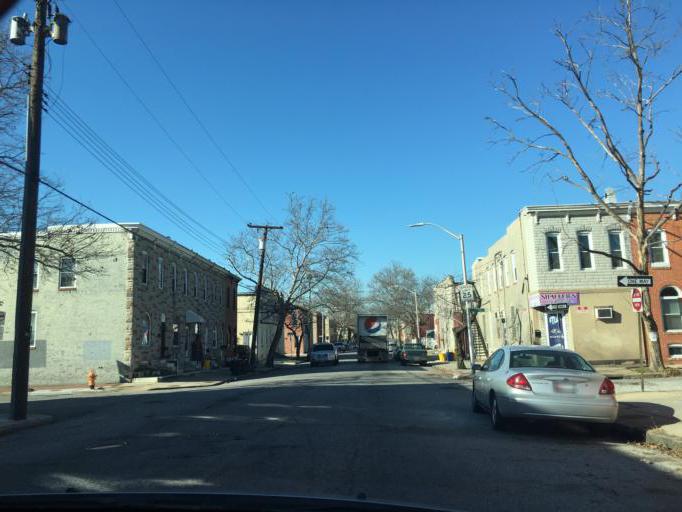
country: US
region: Maryland
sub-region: City of Baltimore
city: Baltimore
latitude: 39.2804
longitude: -76.6321
